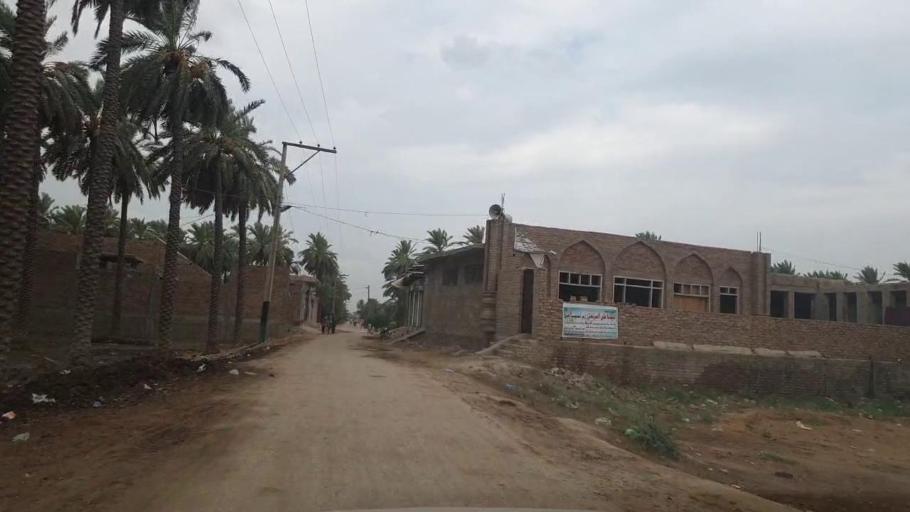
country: PK
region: Sindh
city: Khairpur
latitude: 27.5411
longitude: 68.7474
